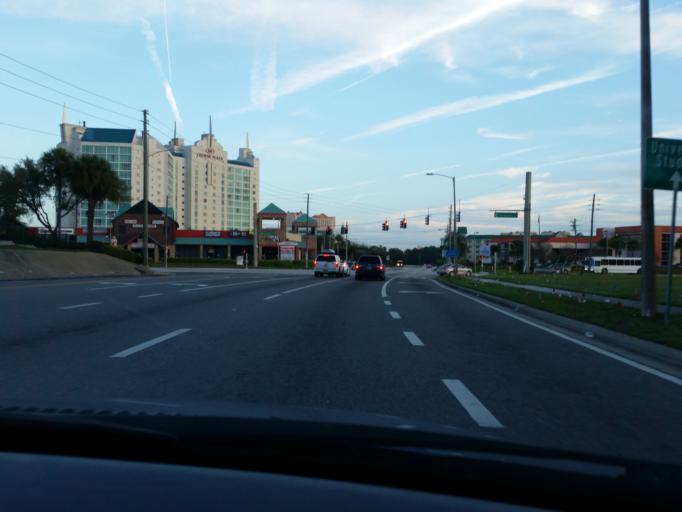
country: US
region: Florida
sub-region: Orange County
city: Tangelo Park
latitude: 28.4492
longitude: -81.4658
